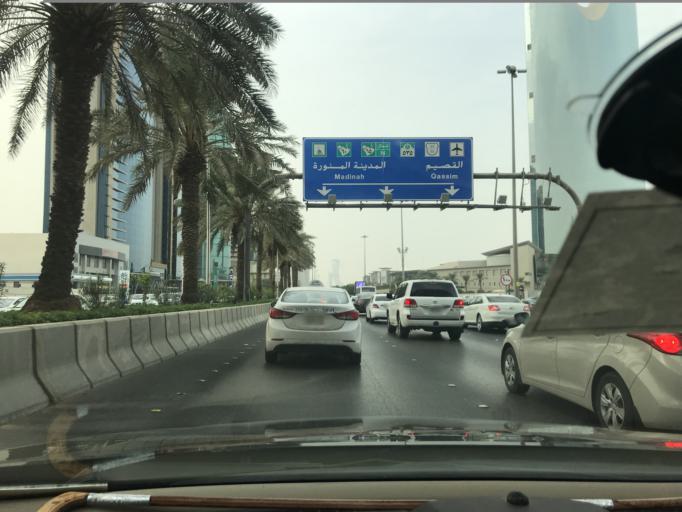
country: SA
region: Ar Riyad
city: Riyadh
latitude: 24.7076
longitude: 46.6744
